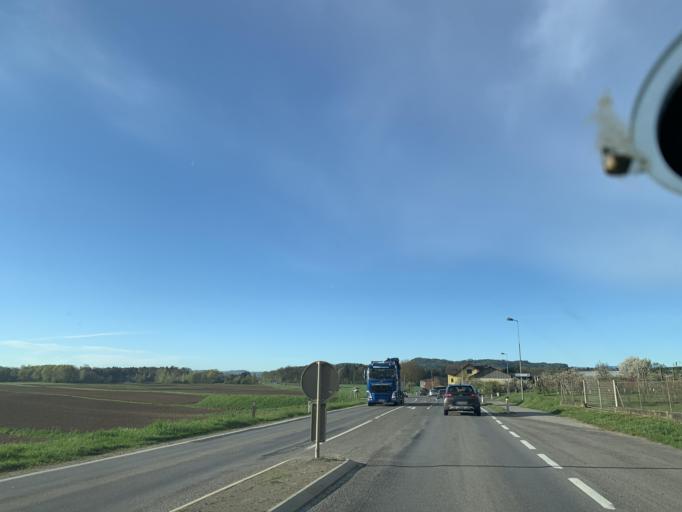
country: AT
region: Styria
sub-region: Politischer Bezirk Leibnitz
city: Lang
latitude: 46.8374
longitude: 15.5174
